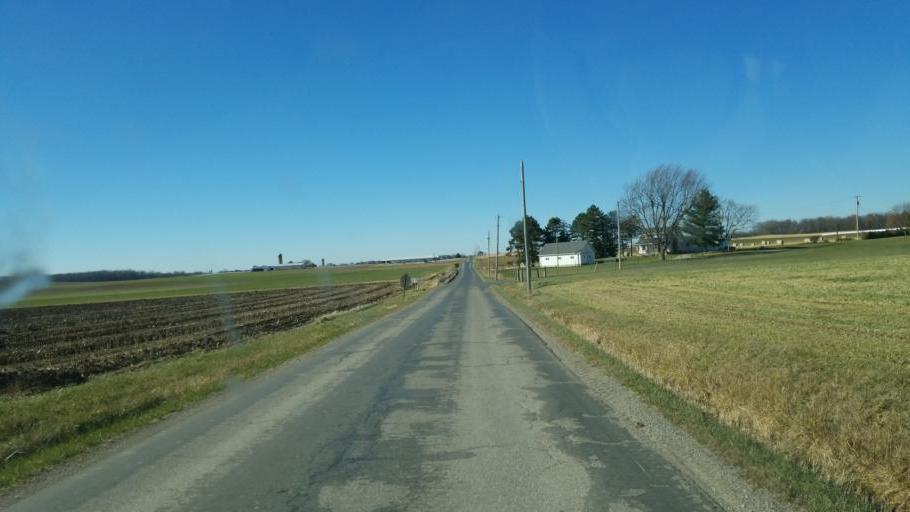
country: US
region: Ohio
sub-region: Huron County
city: Greenwich
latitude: 40.9607
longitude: -82.5415
